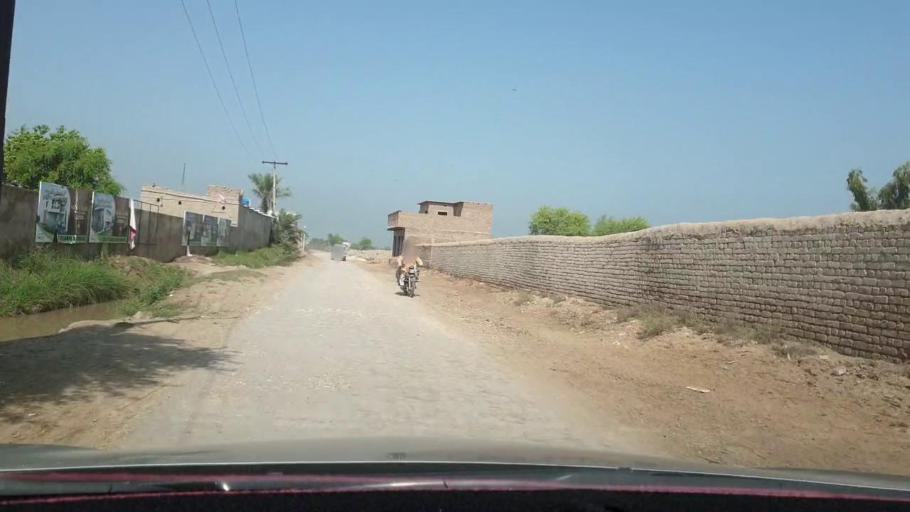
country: PK
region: Sindh
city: Kambar
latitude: 27.5976
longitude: 67.9863
